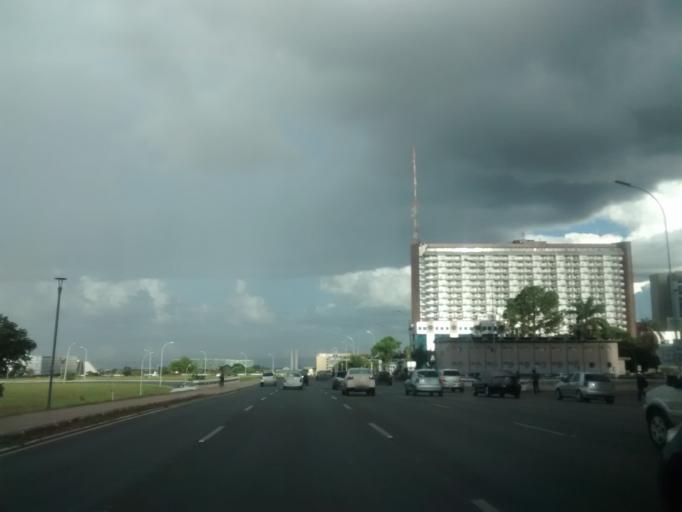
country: BR
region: Federal District
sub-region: Brasilia
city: Brasilia
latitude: -15.7928
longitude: -47.8907
